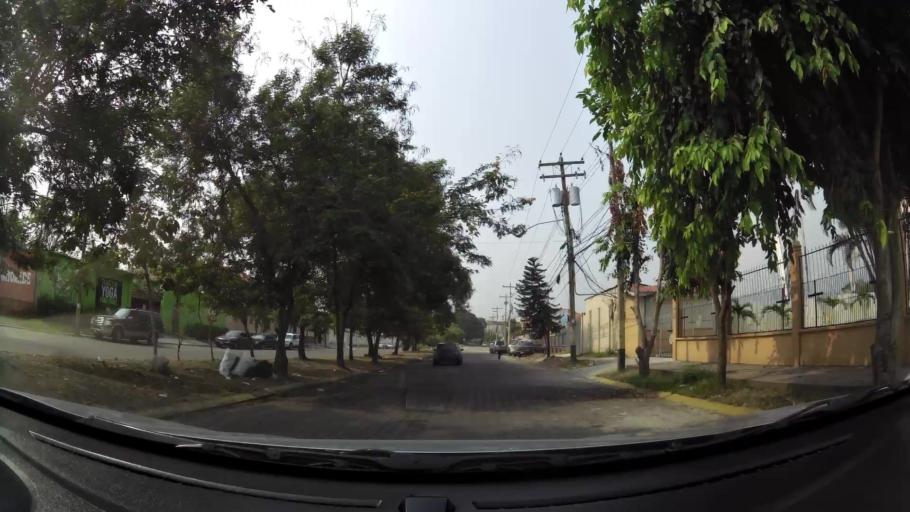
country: HN
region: Cortes
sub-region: San Pedro Sula
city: Pena Blanca
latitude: 15.5350
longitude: -88.0278
